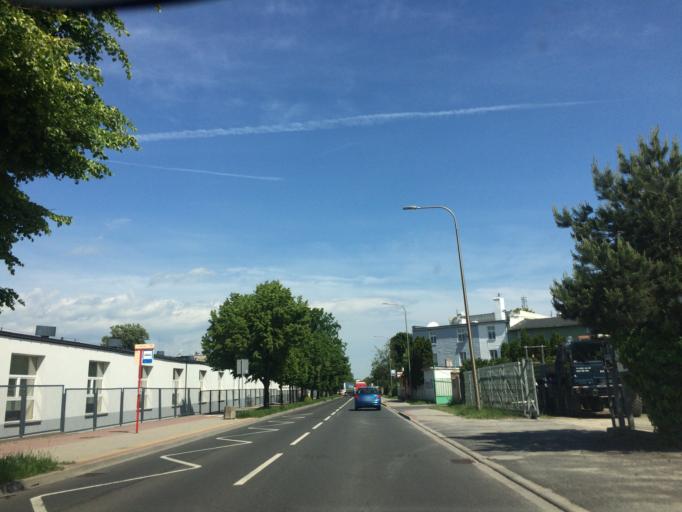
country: PL
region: Lower Silesian Voivodeship
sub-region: Powiat swidnicki
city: Swidnica
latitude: 50.8278
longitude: 16.5008
